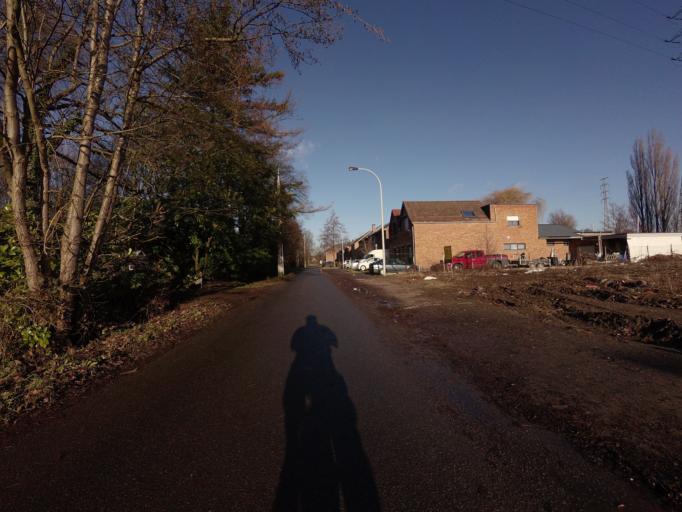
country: BE
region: Flanders
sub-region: Provincie Antwerpen
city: Lier
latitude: 51.1331
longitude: 4.5523
